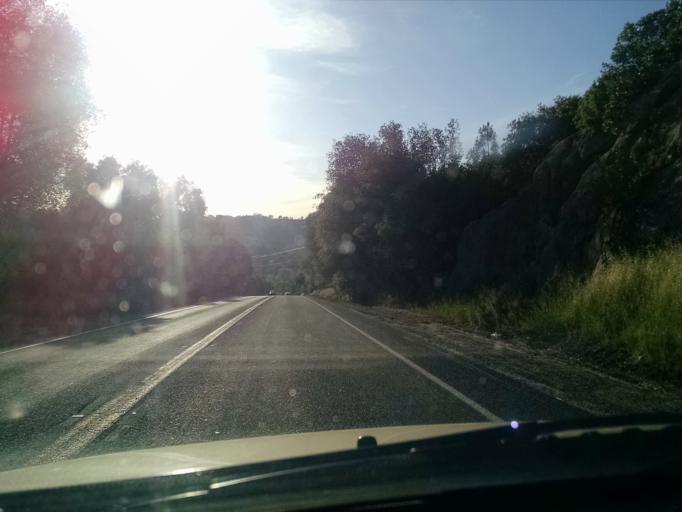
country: US
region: California
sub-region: Mariposa County
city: Mariposa
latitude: 37.4593
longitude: -119.9391
